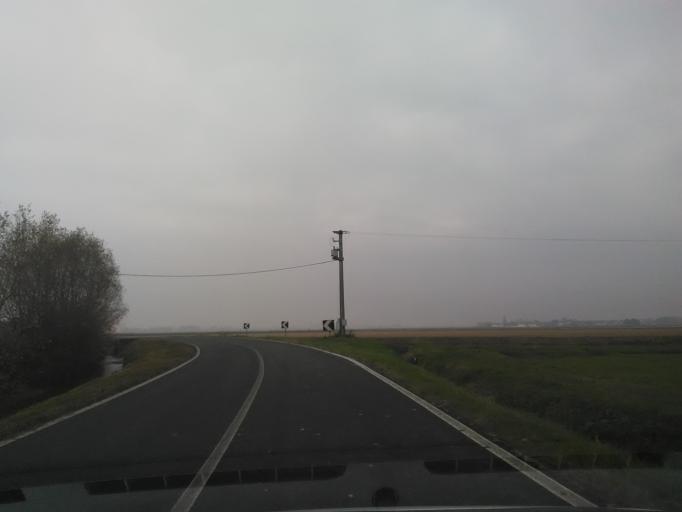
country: IT
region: Piedmont
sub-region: Provincia di Vercelli
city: Salasco
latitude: 45.3163
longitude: 8.2384
